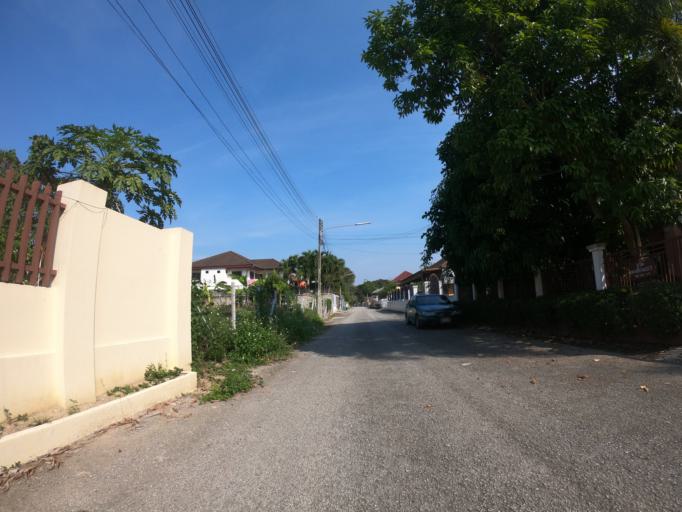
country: TH
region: Chiang Mai
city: Chiang Mai
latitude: 18.8323
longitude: 99.0012
